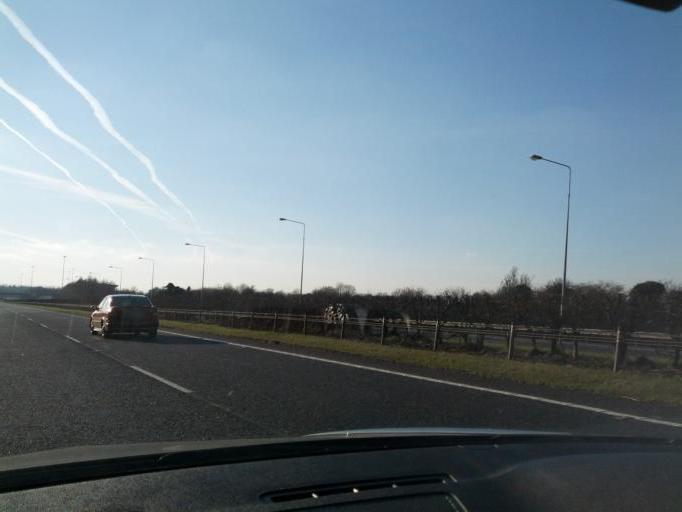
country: IE
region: Leinster
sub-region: Laois
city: Portlaoise
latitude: 53.0133
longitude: -7.2906
